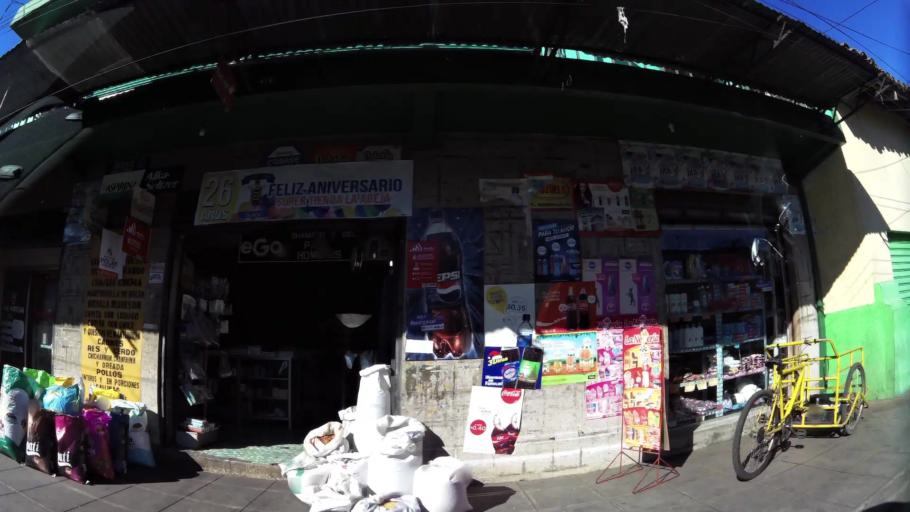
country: SV
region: San Miguel
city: San Miguel
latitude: 13.4773
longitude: -88.1780
